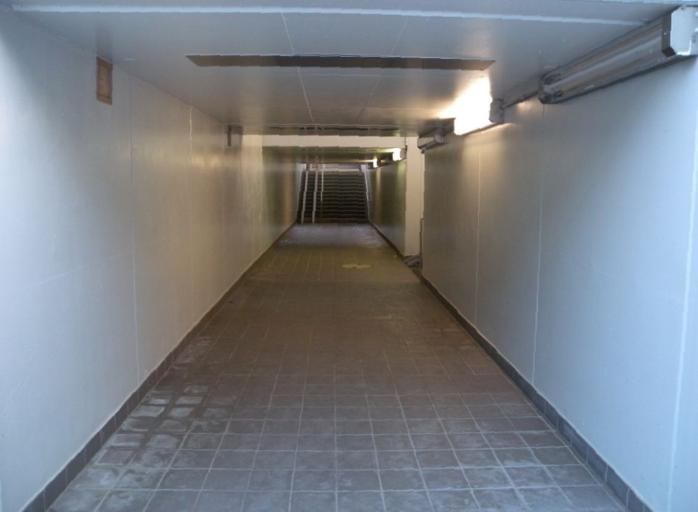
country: DE
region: Baden-Wuerttemberg
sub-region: Regierungsbezirk Stuttgart
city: Bobingen an der Rems
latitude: 48.8225
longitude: 9.9130
